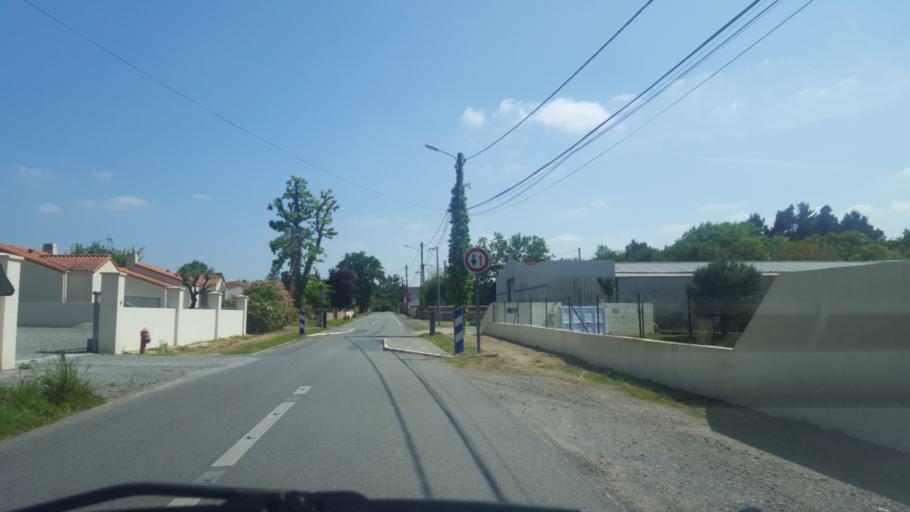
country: FR
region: Pays de la Loire
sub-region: Departement de la Loire-Atlantique
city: La Limouziniere
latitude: 47.0200
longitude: -1.5682
